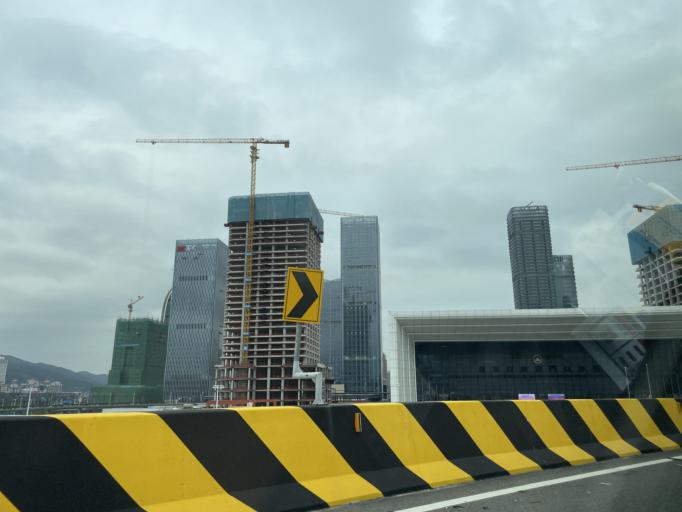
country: MO
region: Macau
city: Macau
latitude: 22.1404
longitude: 113.5465
